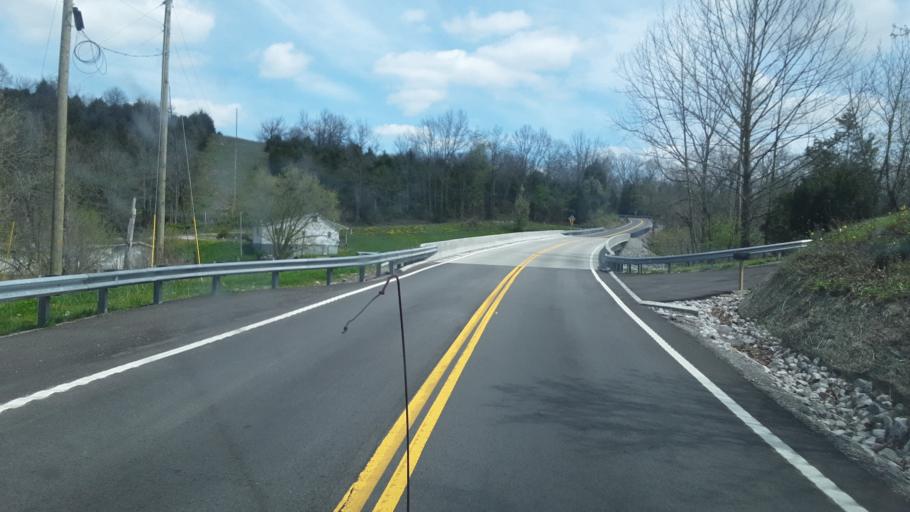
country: US
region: Kentucky
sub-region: Grant County
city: Dry Ridge
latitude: 38.6588
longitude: -84.6731
